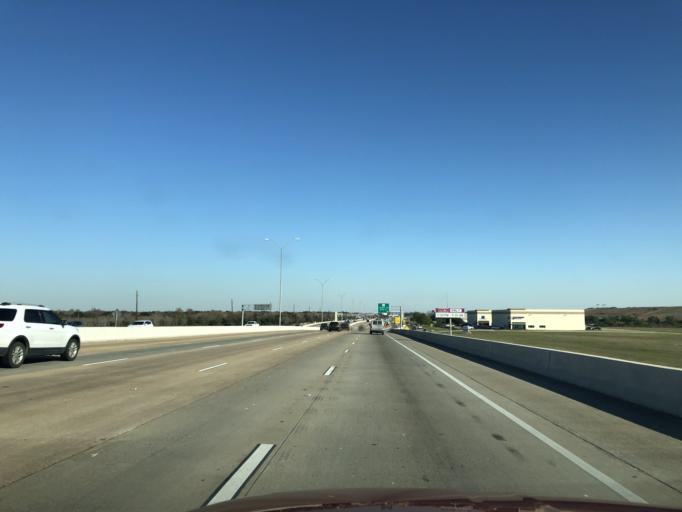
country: US
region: Texas
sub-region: Fort Bend County
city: Fresno
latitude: 29.5963
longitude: -95.4449
